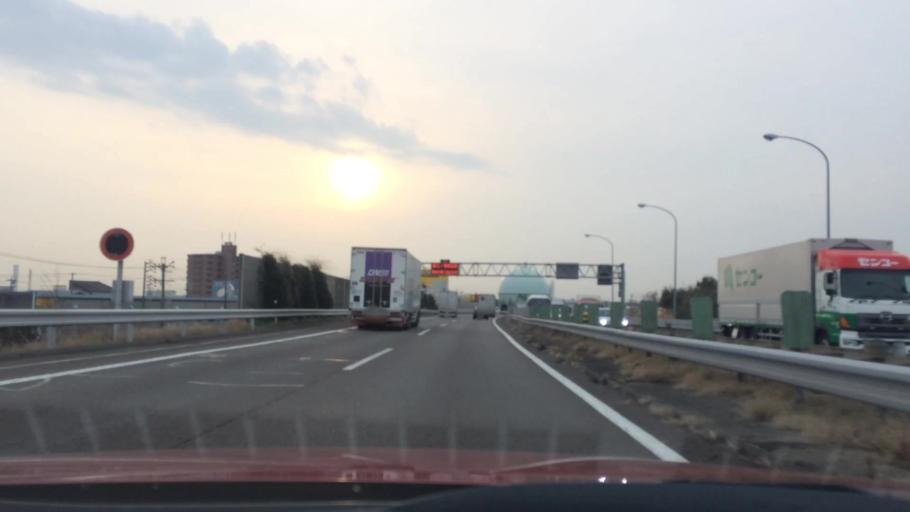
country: JP
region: Aichi
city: Iwakura
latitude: 35.2754
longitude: 136.8433
